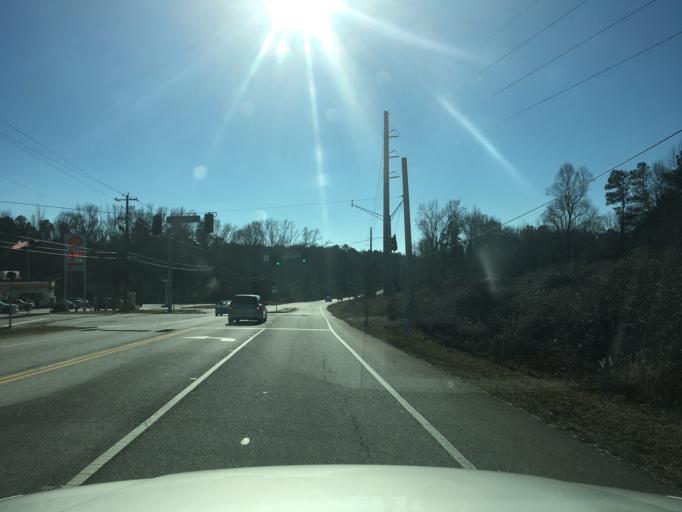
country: US
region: Georgia
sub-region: Carroll County
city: Villa Rica
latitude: 33.7170
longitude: -84.8343
